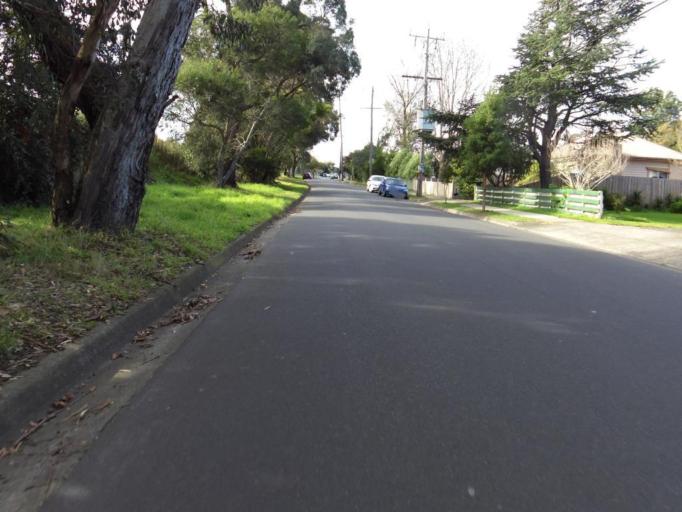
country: AU
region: Victoria
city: Mitcham
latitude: -37.8185
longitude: 145.2213
